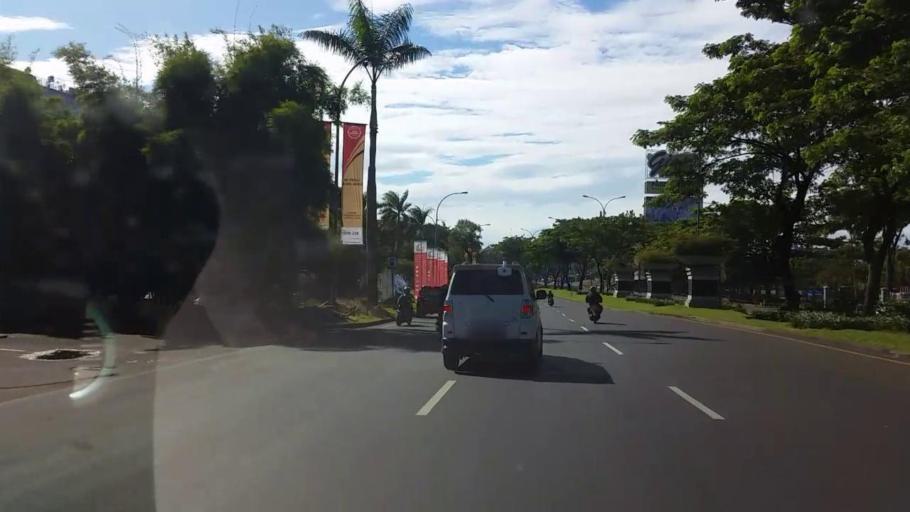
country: ID
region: West Java
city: Serpong
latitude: -6.2972
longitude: 106.6669
